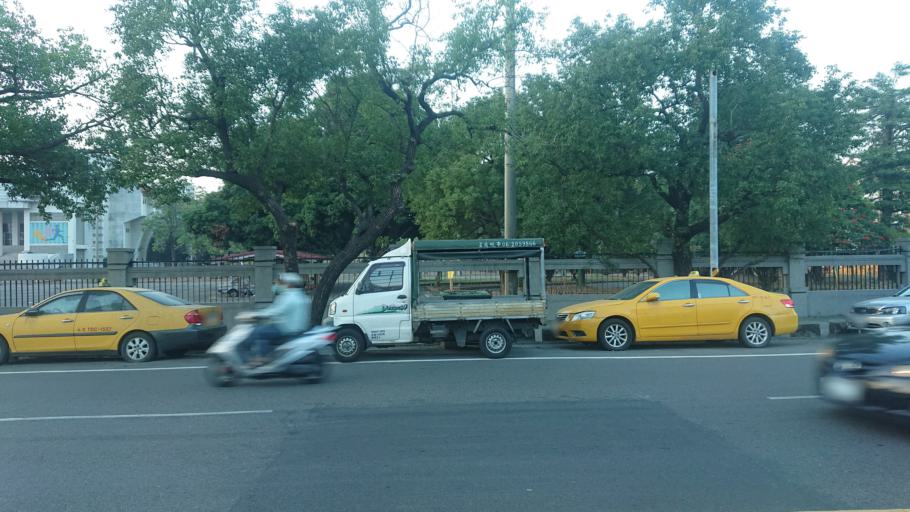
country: TW
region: Taiwan
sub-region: Tainan
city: Tainan
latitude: 23.0147
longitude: 120.2346
